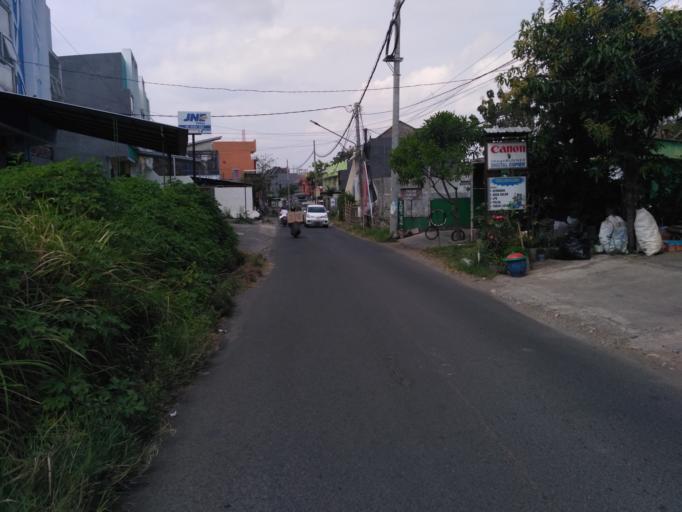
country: ID
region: East Java
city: Malang
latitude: -7.9270
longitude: 112.6060
